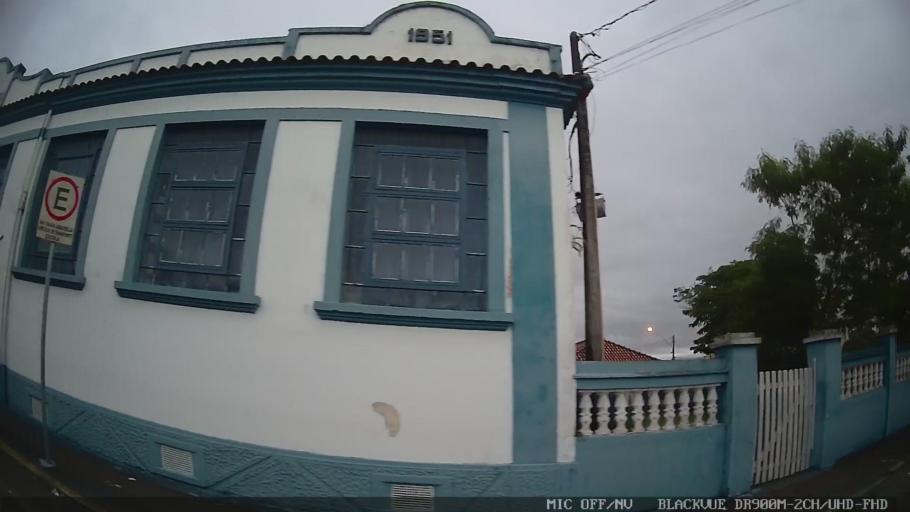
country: BR
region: Sao Paulo
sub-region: Iguape
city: Iguape
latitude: -24.7119
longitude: -47.5594
